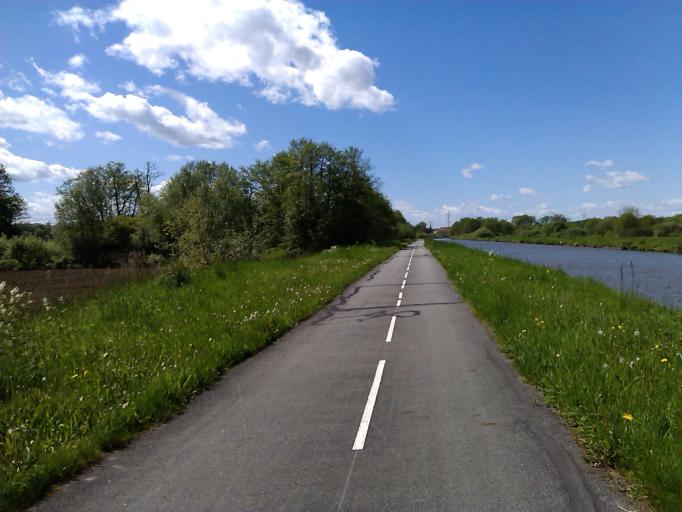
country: FR
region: Franche-Comte
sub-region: Territoire de Belfort
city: Morvillars
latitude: 47.5738
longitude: 6.9543
